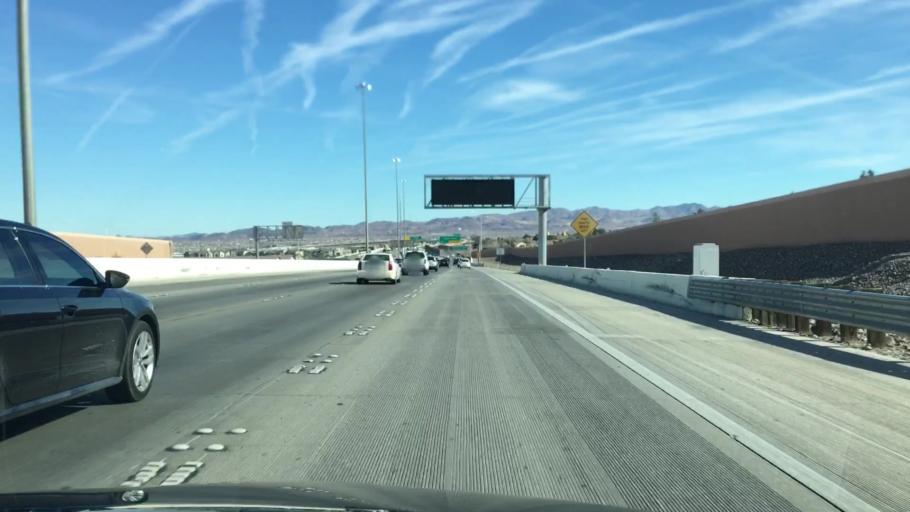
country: US
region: Nevada
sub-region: Clark County
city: Henderson
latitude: 36.0304
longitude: -115.0378
